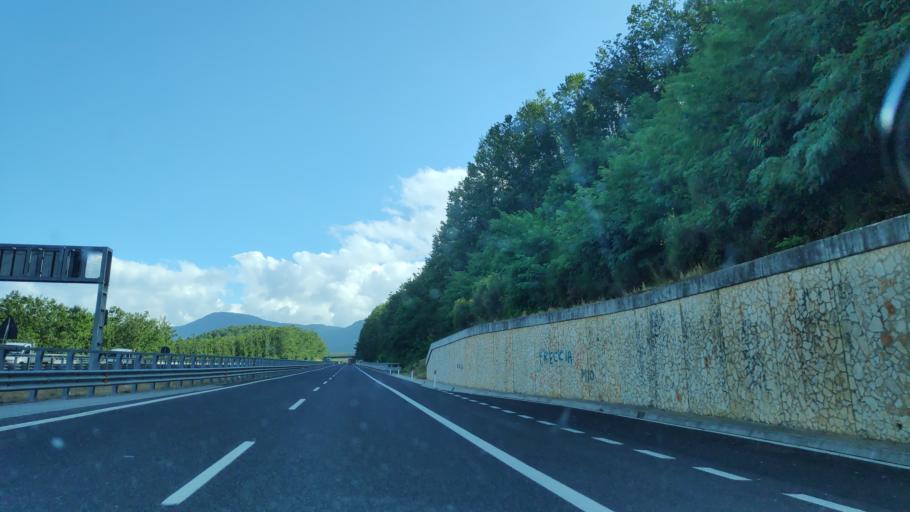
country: IT
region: Campania
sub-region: Provincia di Salerno
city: Buonabitacolo
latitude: 40.2518
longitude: 15.6600
